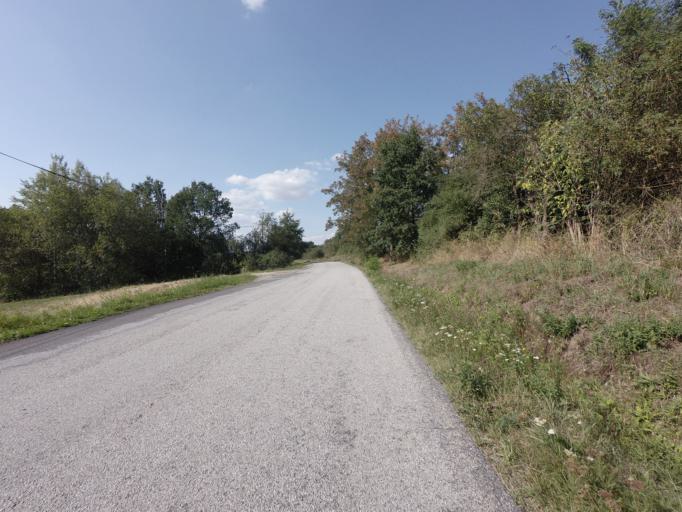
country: CZ
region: Jihocesky
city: Tyn nad Vltavou
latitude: 49.2013
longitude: 14.4457
